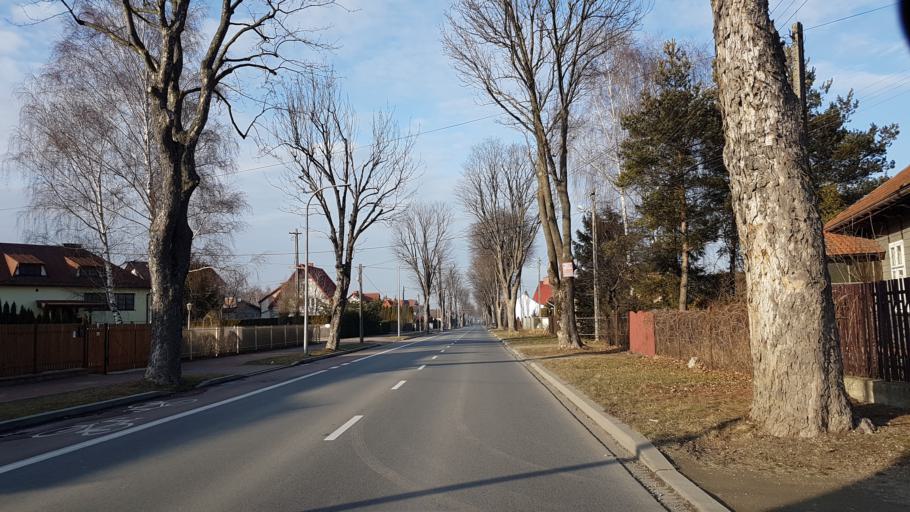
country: PL
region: Lesser Poland Voivodeship
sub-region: Powiat nowosadecki
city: Stary Sacz
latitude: 49.5461
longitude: 20.6427
